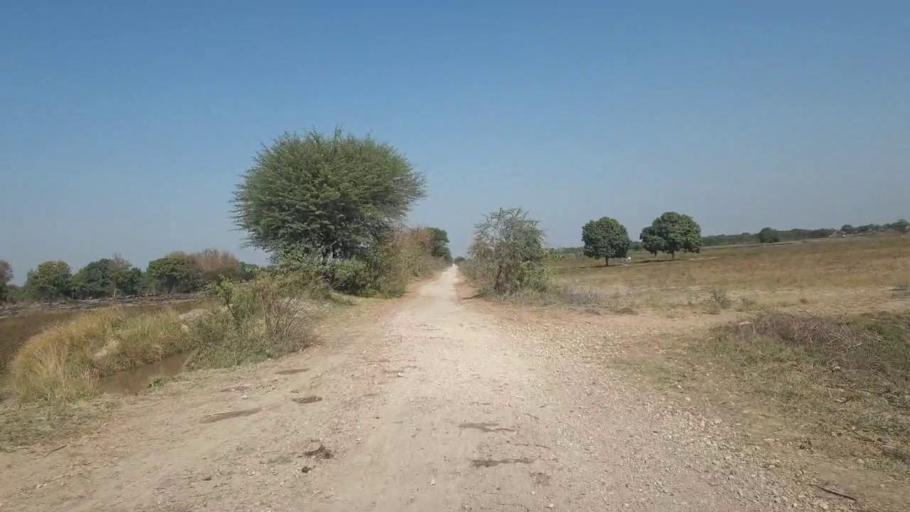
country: PK
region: Sindh
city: Chambar
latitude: 25.3015
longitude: 68.6926
